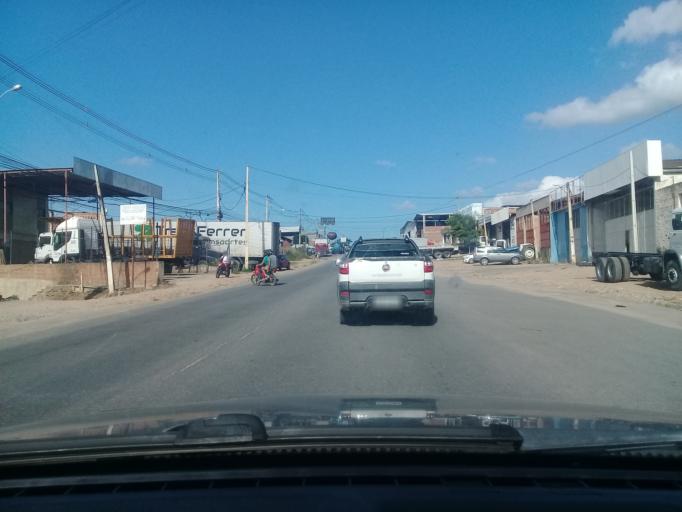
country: BR
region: Pernambuco
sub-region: Vitoria De Santo Antao
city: Vitoria de Santo Antao
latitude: -8.1144
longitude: -35.2810
